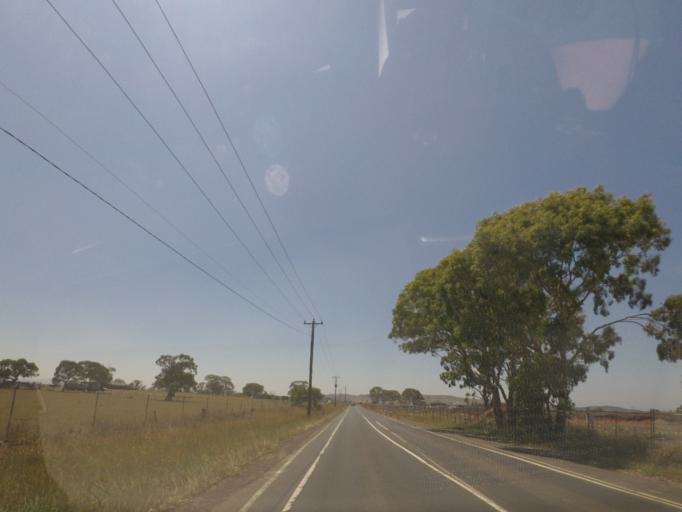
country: AU
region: Victoria
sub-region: Whittlesea
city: Epping
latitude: -37.6073
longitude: 145.0205
